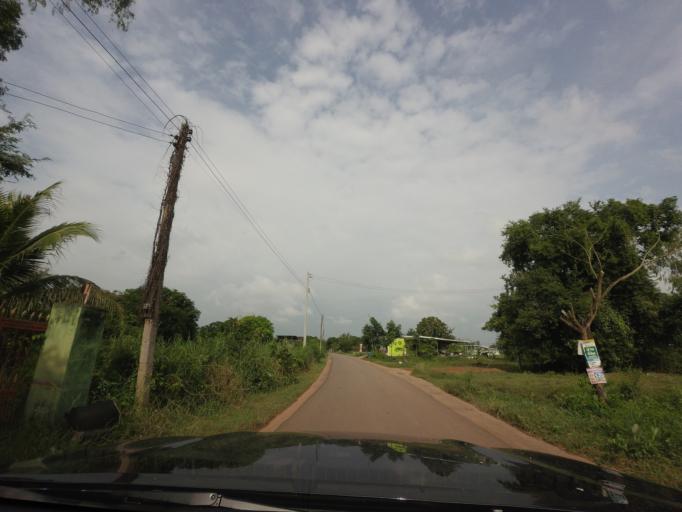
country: TH
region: Nong Khai
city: Nong Khai
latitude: 17.8132
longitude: 102.7272
